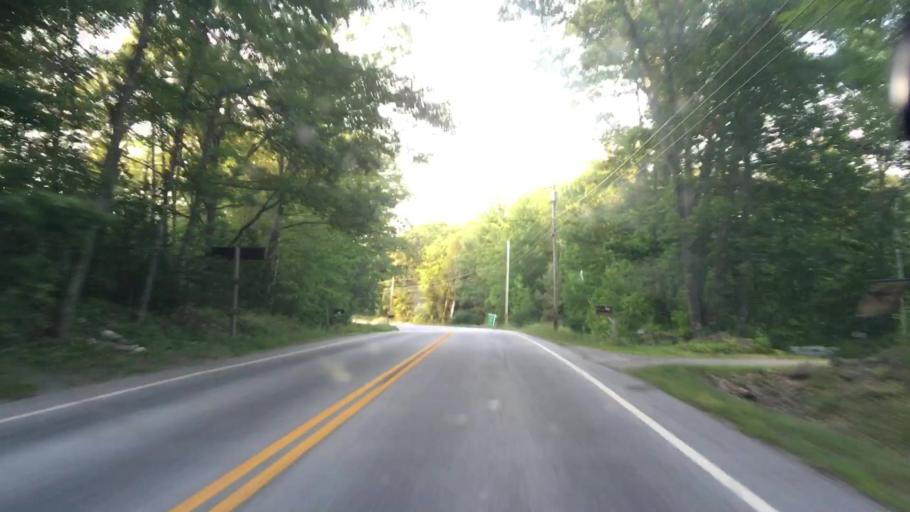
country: US
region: Maine
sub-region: Waldo County
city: Frankfort
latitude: 44.6776
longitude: -68.9194
